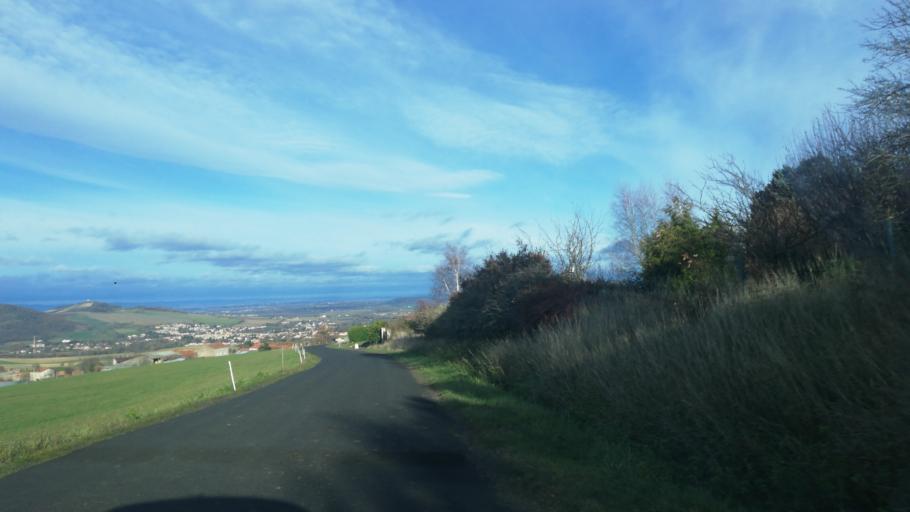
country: FR
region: Auvergne
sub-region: Departement du Puy-de-Dome
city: Billom
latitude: 45.6963
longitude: 3.3573
